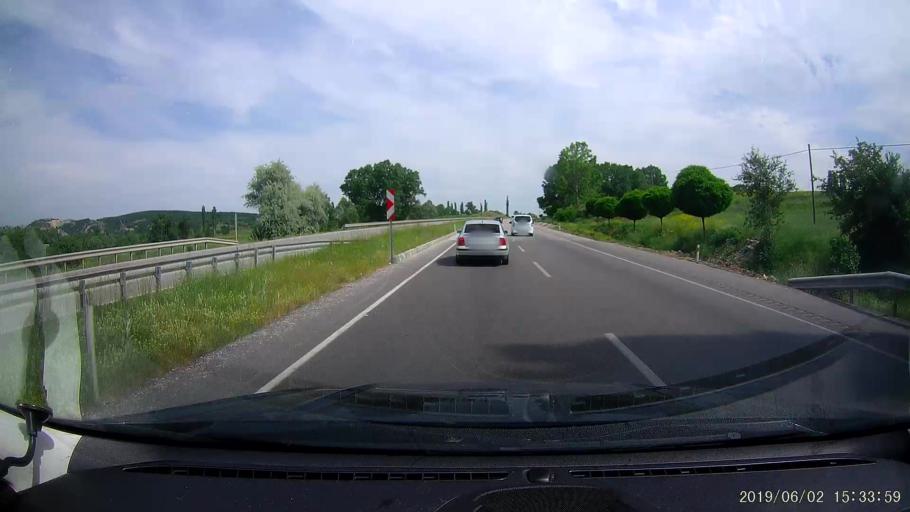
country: TR
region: Amasya
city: Saraycik
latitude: 40.9185
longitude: 35.1693
